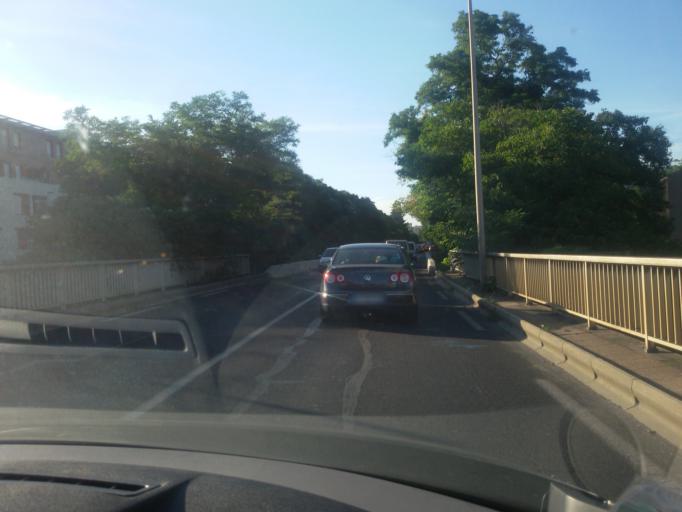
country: FR
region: Languedoc-Roussillon
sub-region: Departement de l'Herault
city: Montpellier
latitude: 43.6013
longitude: 3.8680
